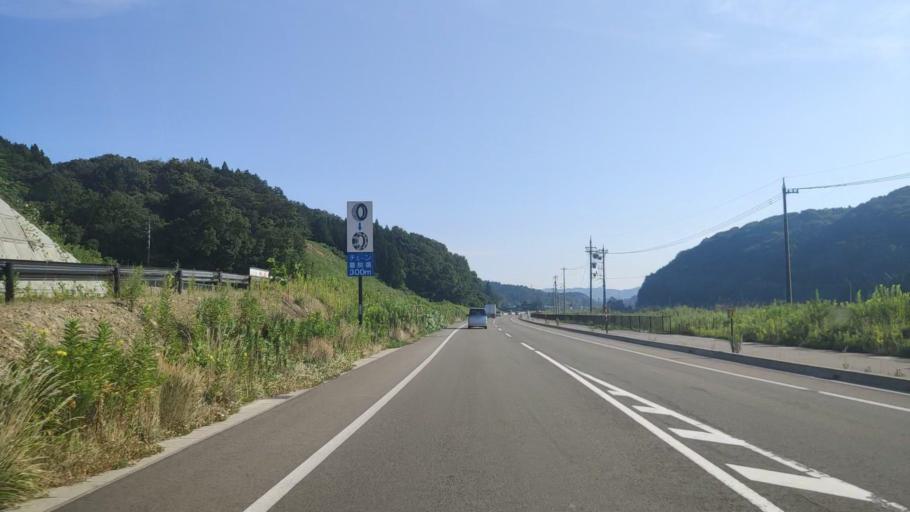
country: JP
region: Fukui
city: Maruoka
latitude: 36.2080
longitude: 136.2686
